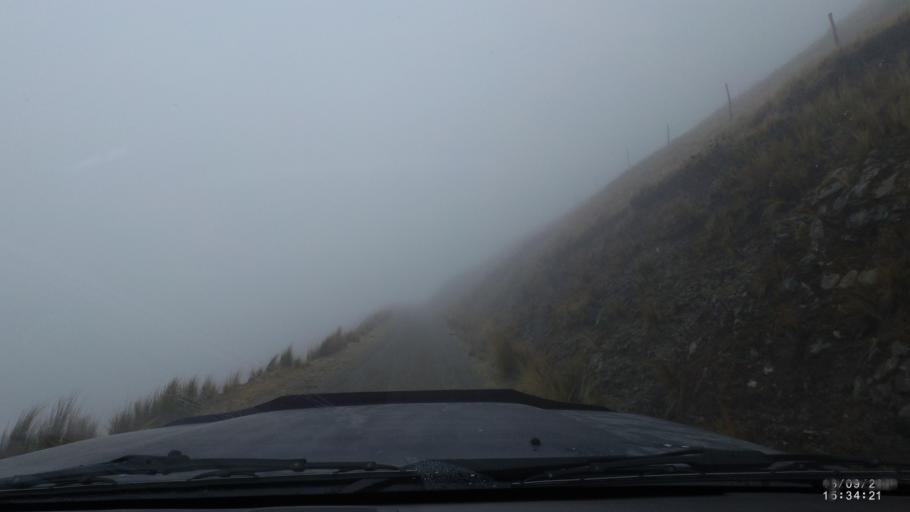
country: BO
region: Cochabamba
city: Colomi
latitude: -17.3359
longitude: -65.7395
